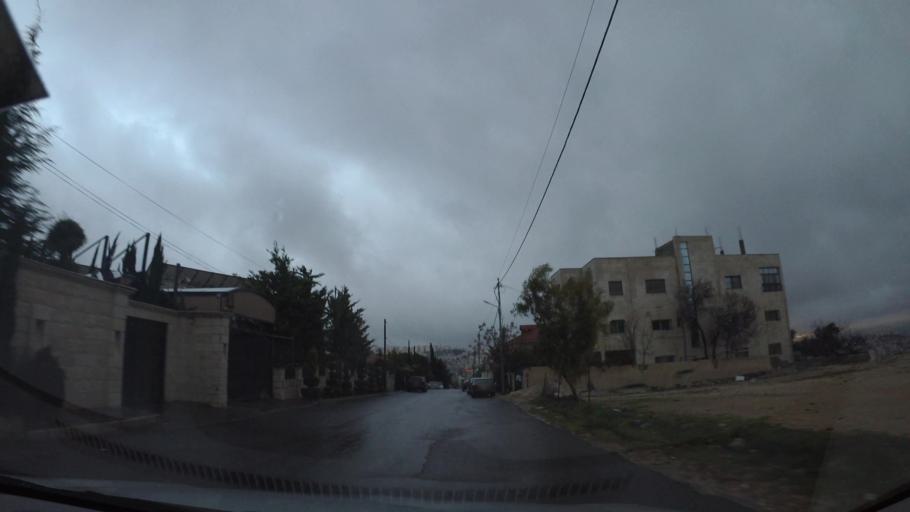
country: JO
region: Amman
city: Al Jubayhah
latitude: 32.0301
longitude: 35.8473
